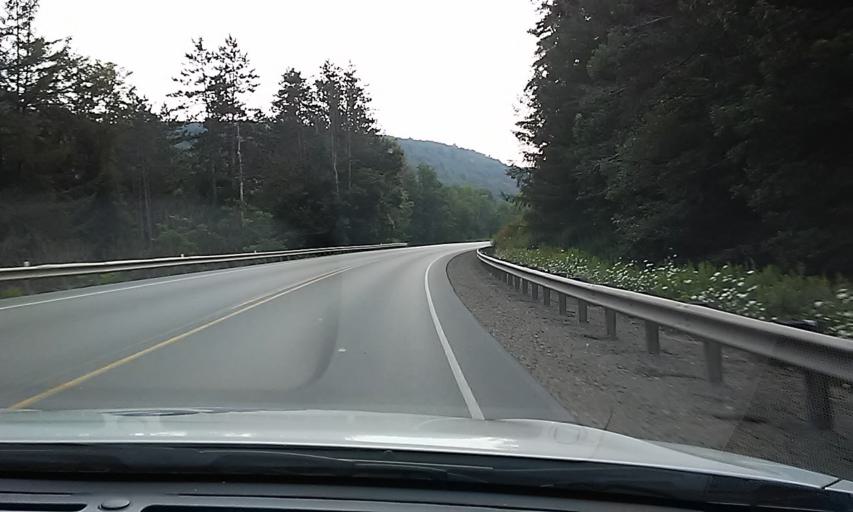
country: US
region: Pennsylvania
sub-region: Potter County
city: Coudersport
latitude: 41.7578
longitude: -77.9016
